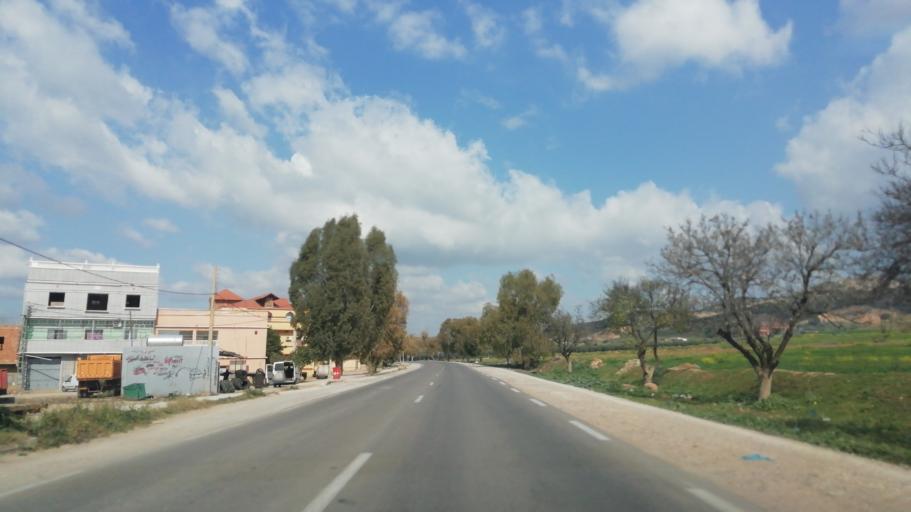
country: DZ
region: Mostaganem
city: Mostaganem
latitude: 35.6860
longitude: 0.2089
